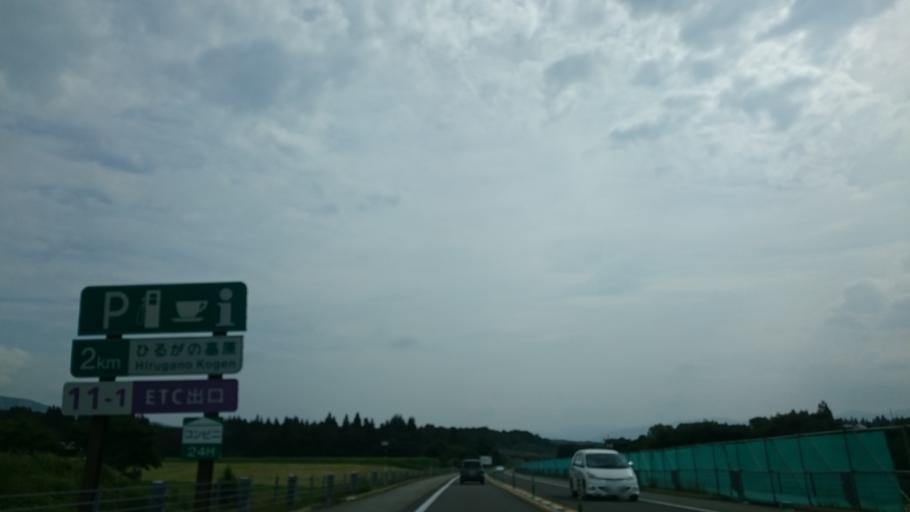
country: JP
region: Gifu
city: Gujo
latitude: 36.0013
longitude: 136.9267
